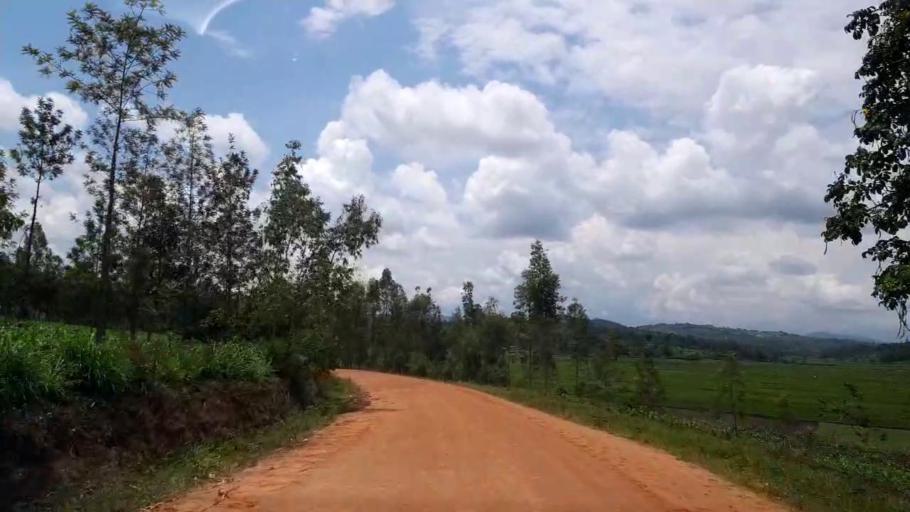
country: RW
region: Northern Province
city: Byumba
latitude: -1.5678
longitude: 30.2982
